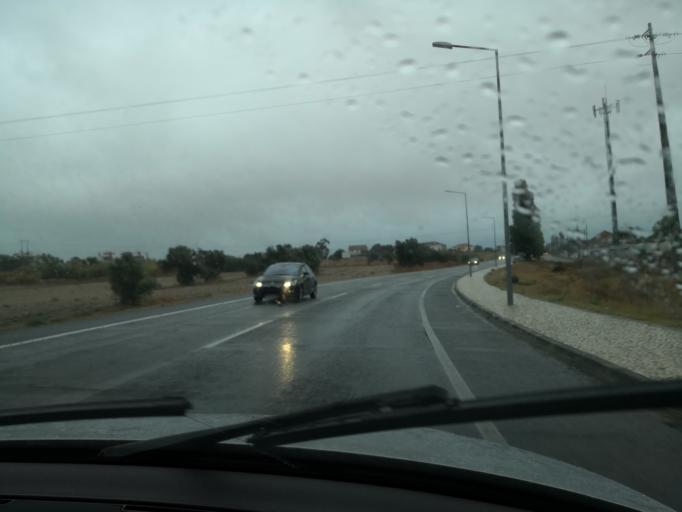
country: PT
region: Setubal
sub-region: Moita
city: Moita
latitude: 38.6465
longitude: -8.9827
